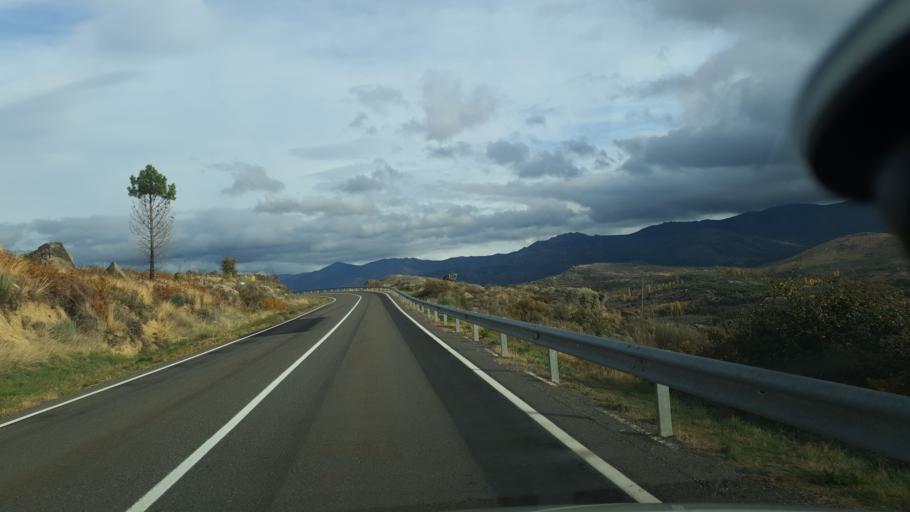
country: ES
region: Castille and Leon
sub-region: Provincia de Avila
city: Hoyocasero
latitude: 40.3918
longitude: -4.9567
